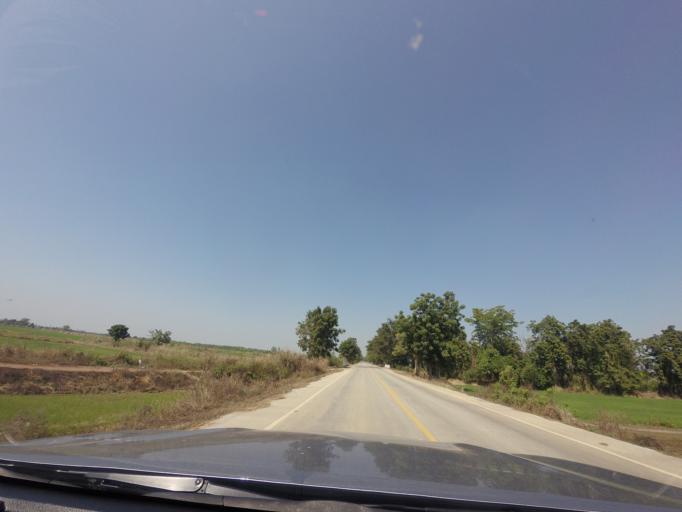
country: TH
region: Sukhothai
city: Ban Na
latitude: 17.1003
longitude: 99.7838
